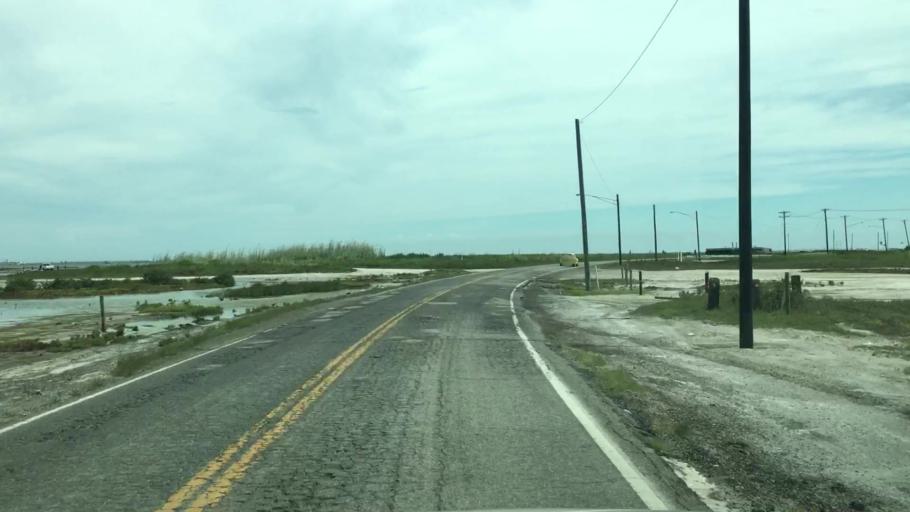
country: US
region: Texas
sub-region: Nueces County
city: Corpus Christi
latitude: 27.6600
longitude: -97.2774
